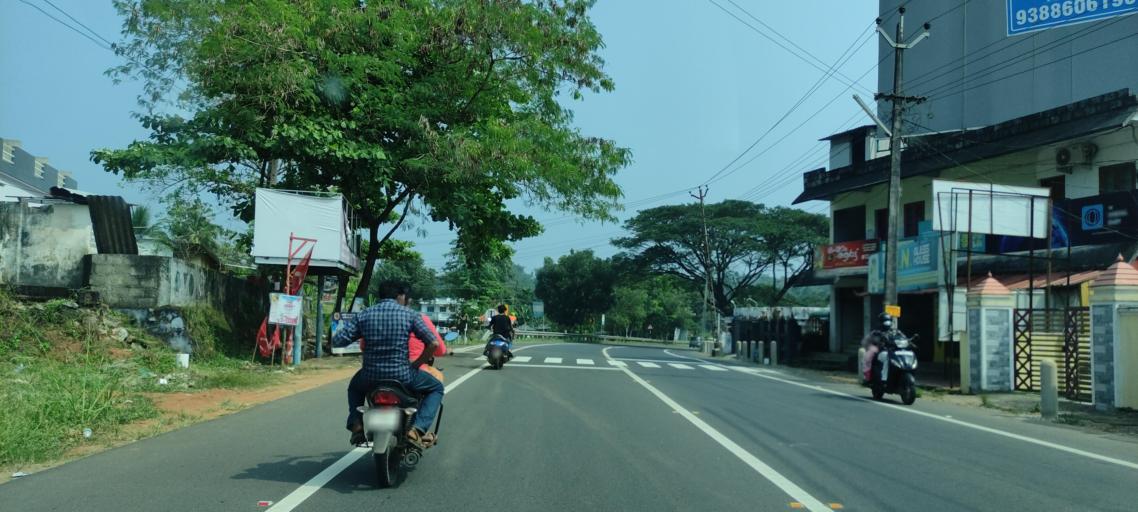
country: IN
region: Kerala
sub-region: Alappuzha
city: Chengannur
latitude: 9.2498
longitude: 76.6662
